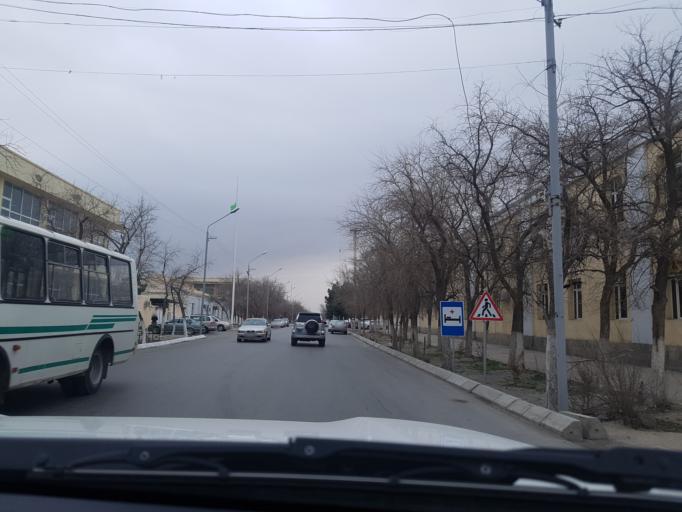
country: TM
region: Balkan
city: Balkanabat
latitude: 39.5034
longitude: 54.3644
